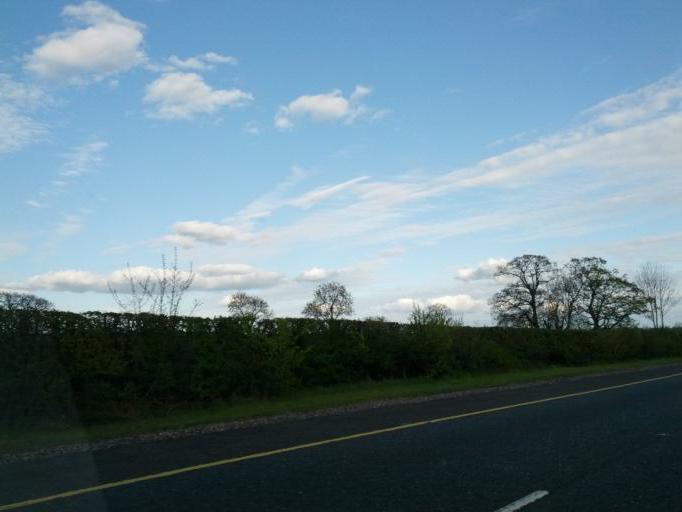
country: IE
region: Leinster
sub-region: Kildare
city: Kilcock
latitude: 53.3884
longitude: -6.6702
